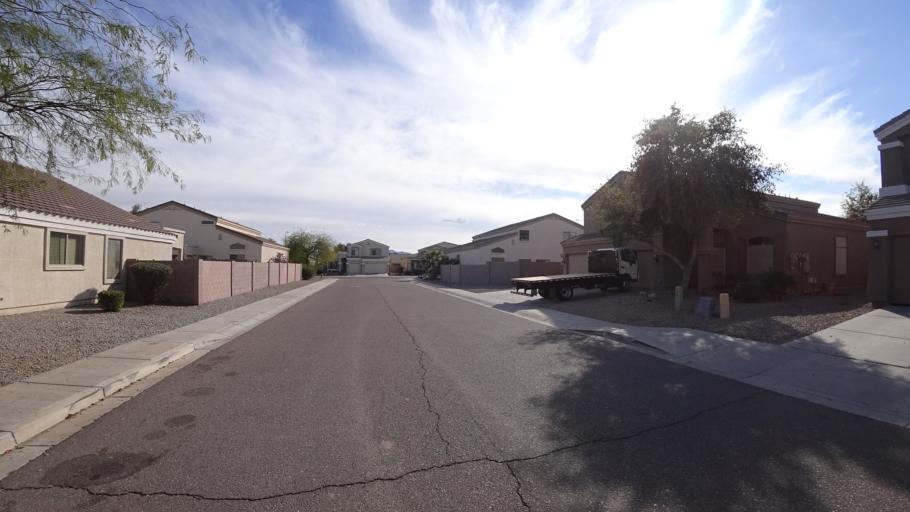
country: US
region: Arizona
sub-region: Maricopa County
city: Tolleson
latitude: 33.4308
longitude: -112.2867
